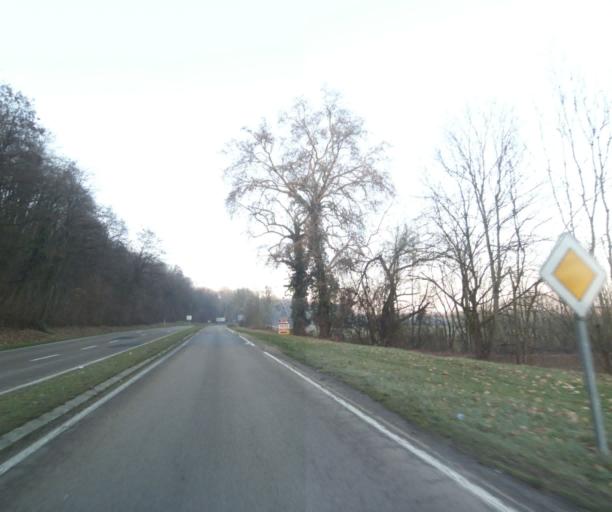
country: FR
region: Champagne-Ardenne
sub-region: Departement de la Haute-Marne
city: Bienville
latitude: 48.5925
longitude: 5.0313
